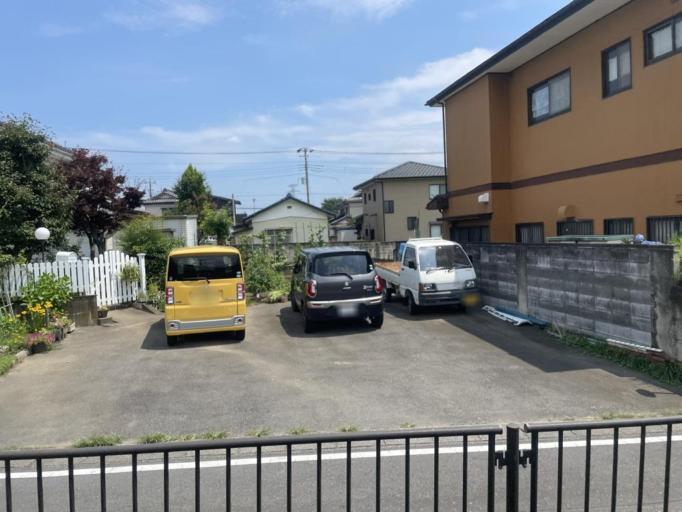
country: JP
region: Gunma
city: Maebashi-shi
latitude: 36.3963
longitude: 139.1166
